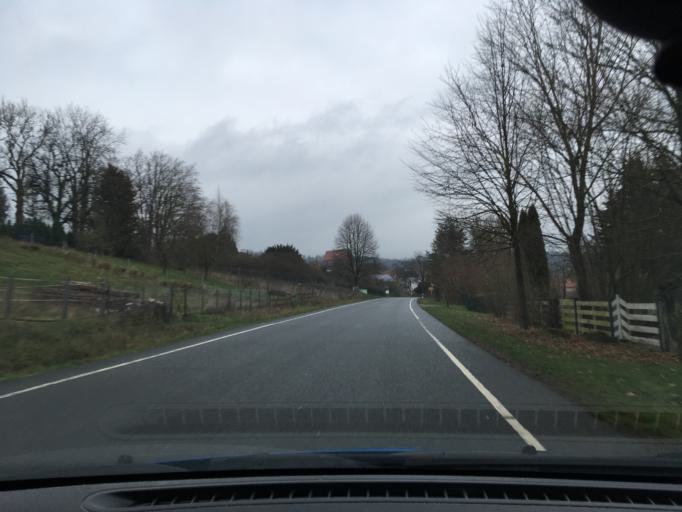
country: DE
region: Lower Saxony
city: Hardegsen
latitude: 51.6474
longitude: 9.8235
